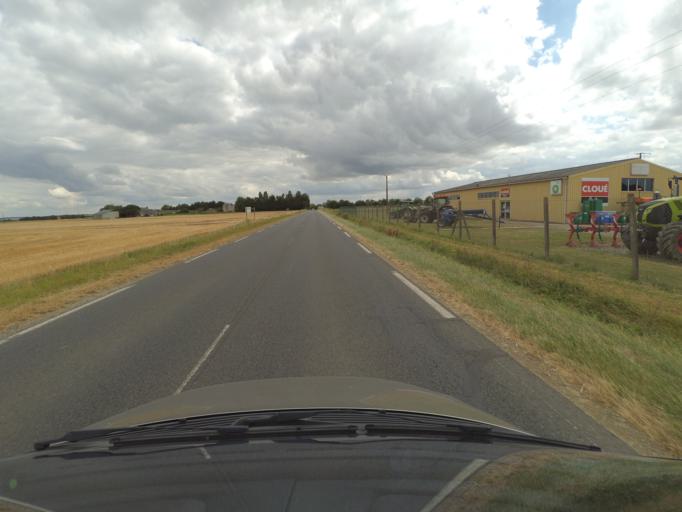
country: FR
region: Centre
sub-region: Departement d'Indre-et-Loire
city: Richelieu
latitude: 47.0079
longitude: 0.2641
